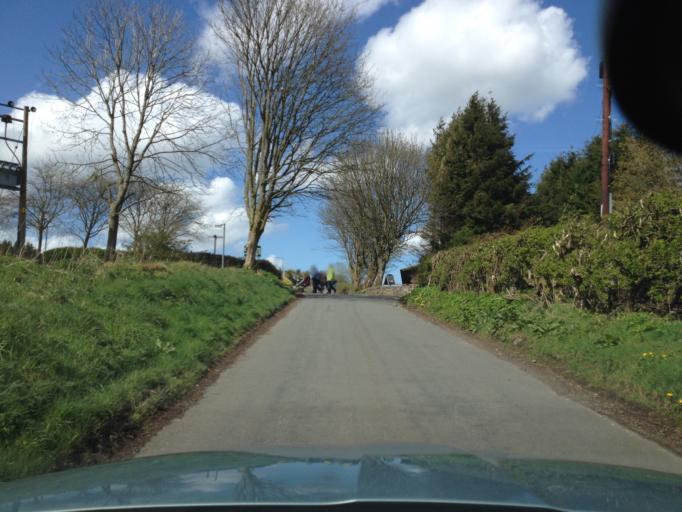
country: GB
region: Scotland
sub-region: West Lothian
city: Linlithgow
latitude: 55.9536
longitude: -3.5930
